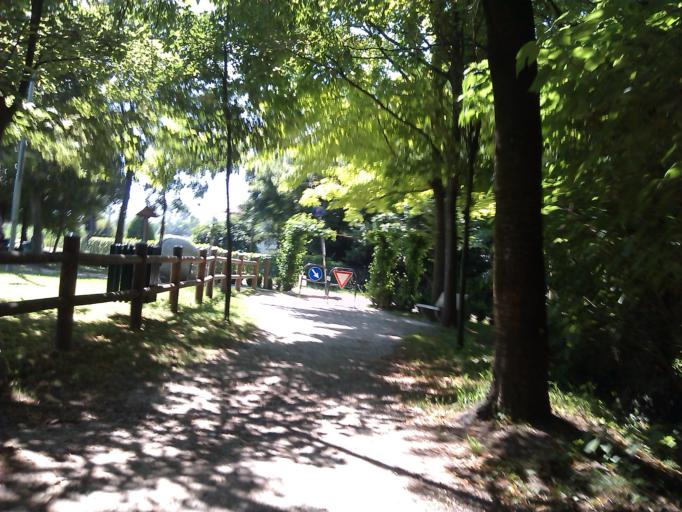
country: IT
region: Veneto
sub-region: Provincia di Treviso
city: Castello di Godego
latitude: 45.6904
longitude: 11.8866
